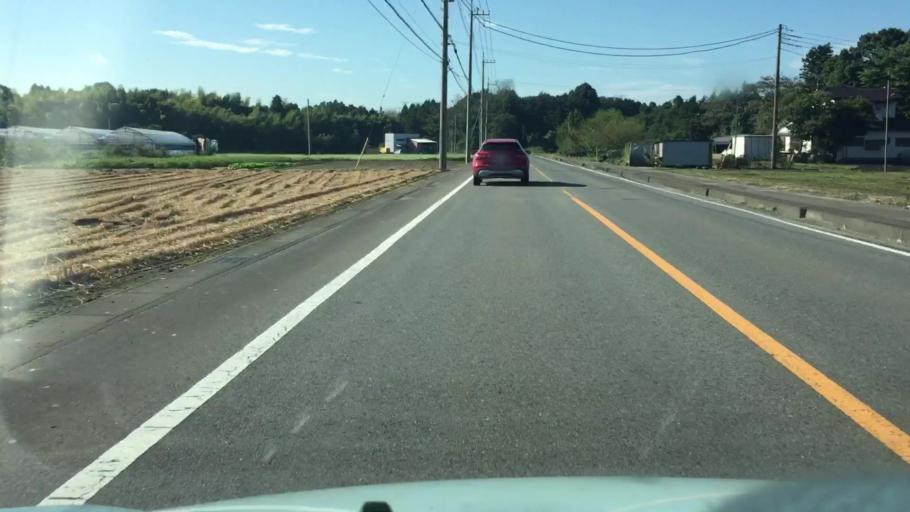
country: JP
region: Tochigi
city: Utsunomiya-shi
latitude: 36.5788
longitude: 139.9806
